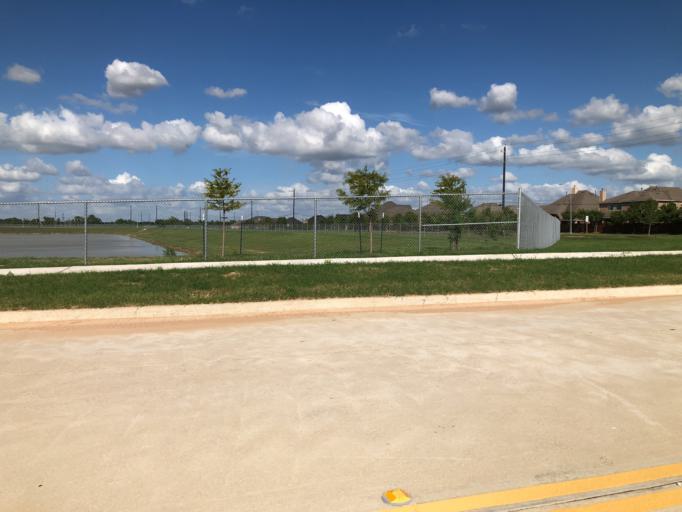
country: US
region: Texas
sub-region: Harris County
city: Katy
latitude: 29.8390
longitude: -95.7792
